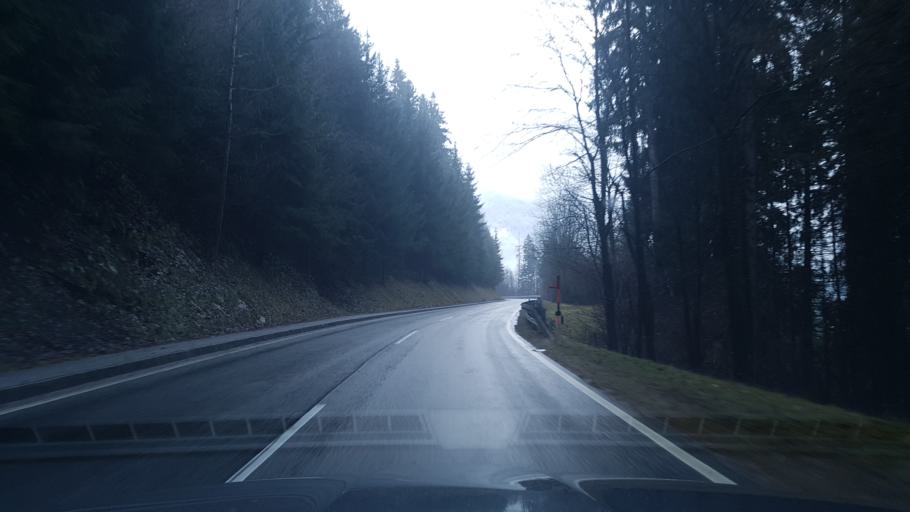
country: AT
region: Salzburg
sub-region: Politischer Bezirk Sankt Johann im Pongau
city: Sankt Johann im Pongau
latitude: 47.3263
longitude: 13.1964
